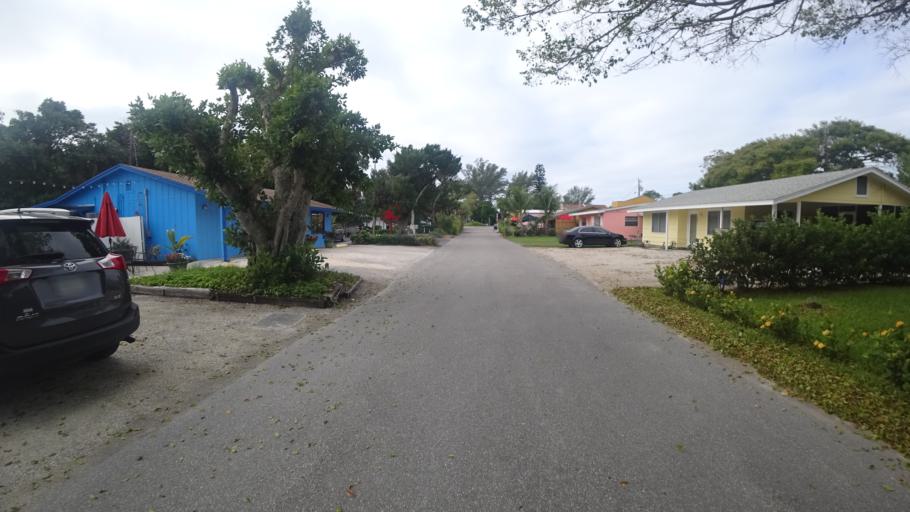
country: US
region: Florida
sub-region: Manatee County
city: Longboat Key
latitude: 27.4145
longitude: -82.6595
